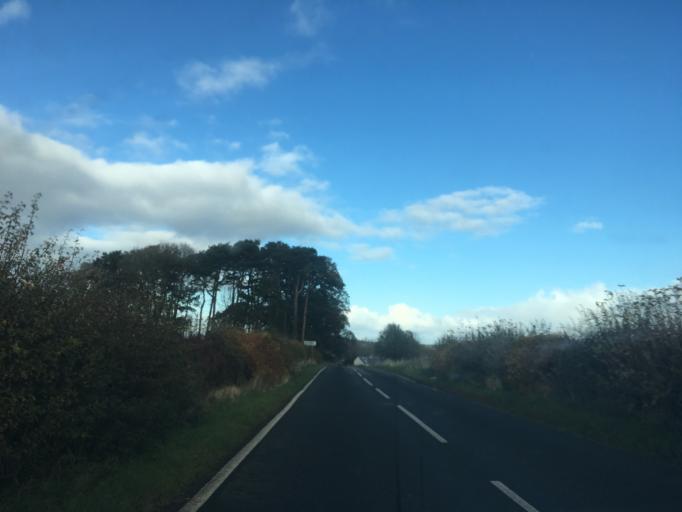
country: GB
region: Scotland
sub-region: East Lothian
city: Pencaitland
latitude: 55.8515
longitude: -2.8721
